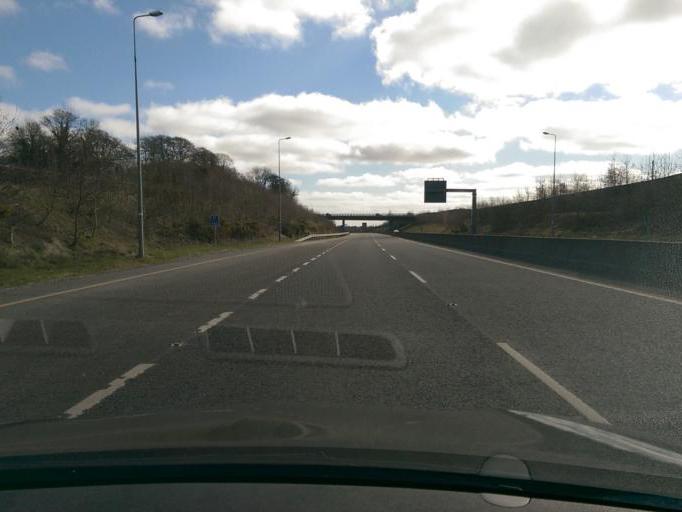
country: IE
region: Leinster
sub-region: An Iarmhi
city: Moate
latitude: 53.3917
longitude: -7.7738
